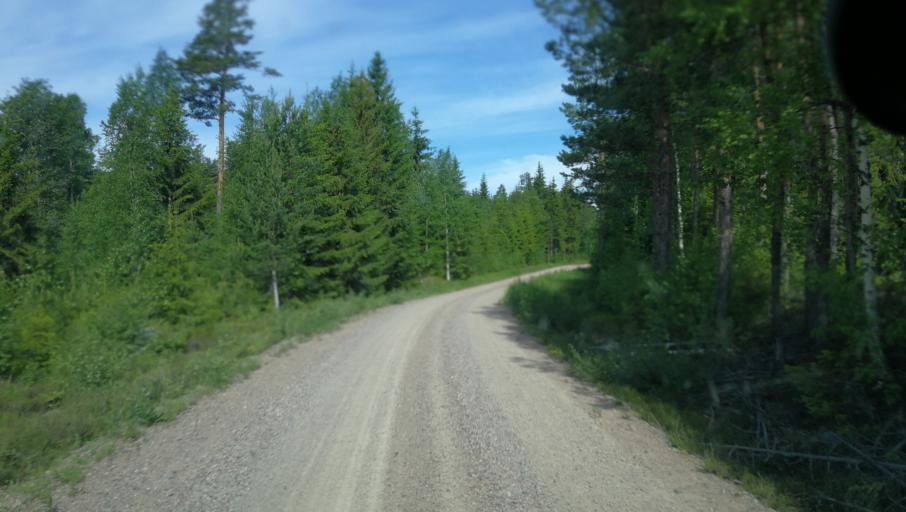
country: SE
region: Dalarna
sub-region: Vansbro Kommun
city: Vansbro
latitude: 60.8215
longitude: 14.1694
